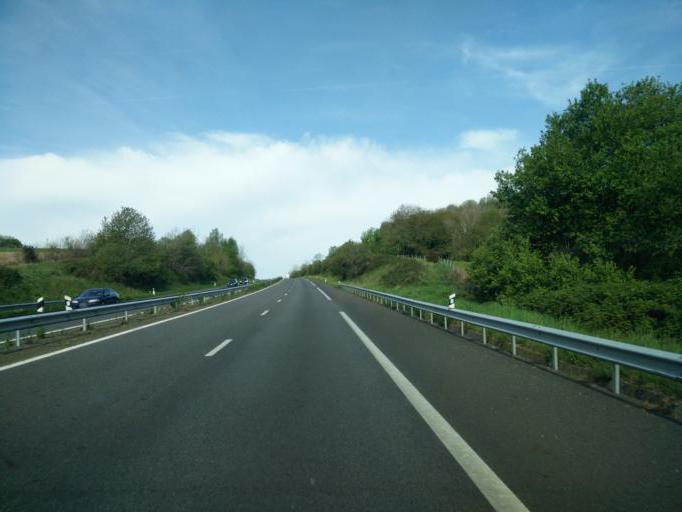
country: FR
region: Brittany
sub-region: Departement d'Ille-et-Vilaine
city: Pleine-Fougeres
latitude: 48.5660
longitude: -1.5661
